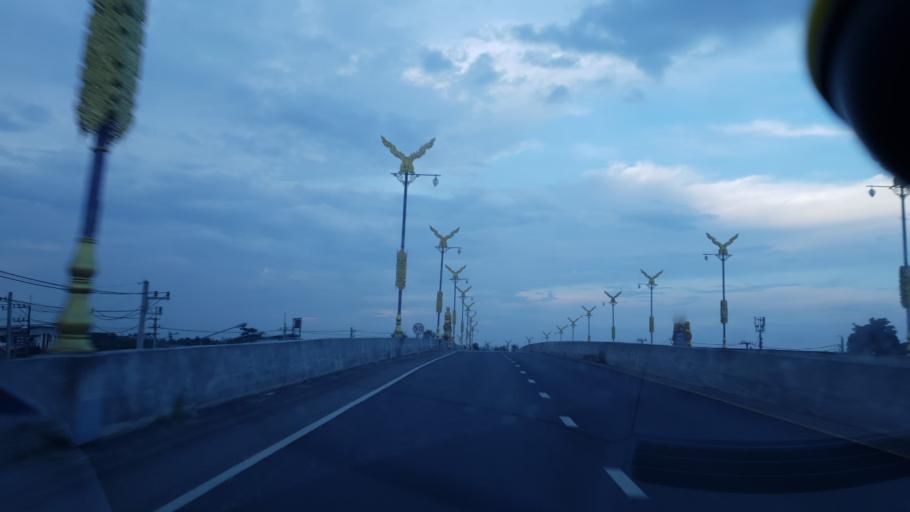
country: TH
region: Chiang Rai
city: Chiang Rai
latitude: 19.8601
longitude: 99.8405
